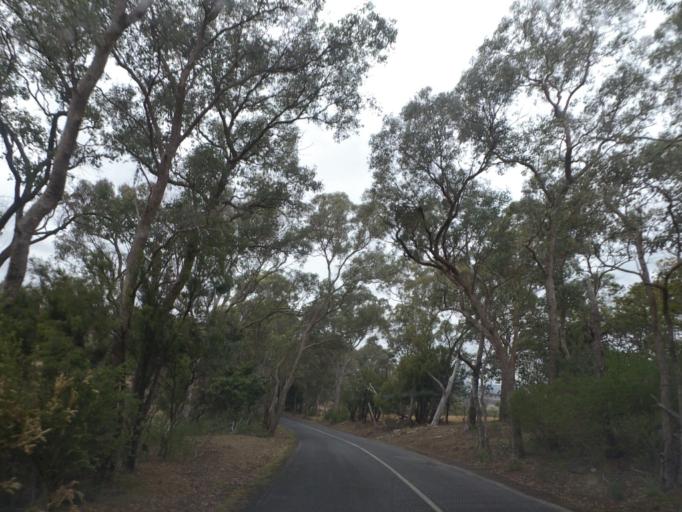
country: AU
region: Victoria
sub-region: Nillumbik
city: North Warrandyte
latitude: -37.6970
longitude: 145.2497
